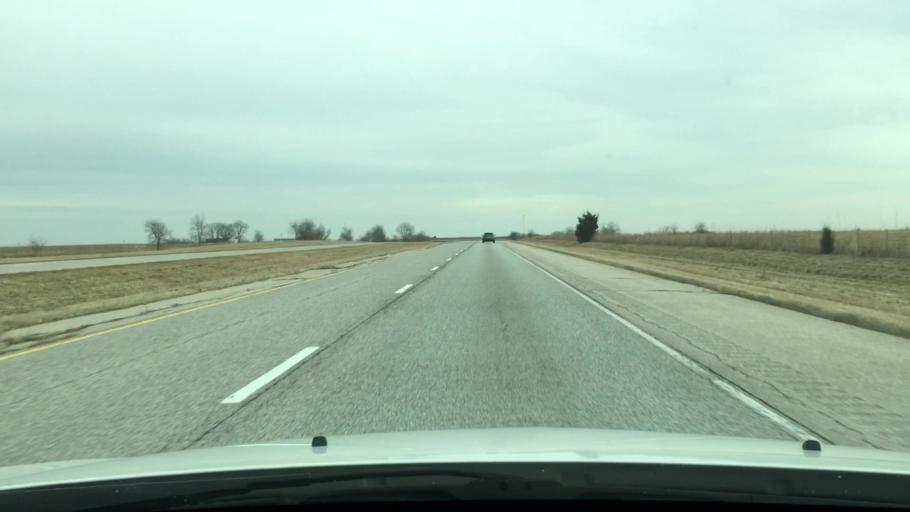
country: US
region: Illinois
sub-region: Pike County
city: Griggsville
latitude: 39.6782
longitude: -90.7121
